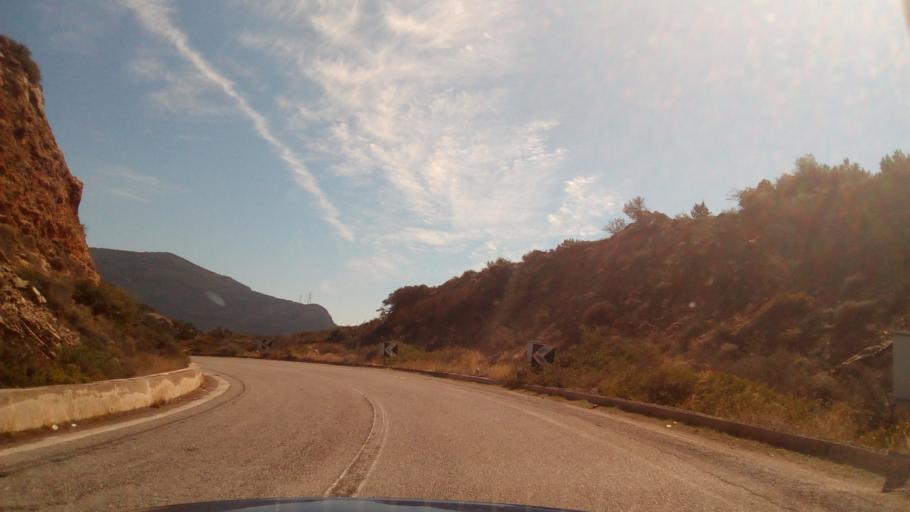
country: GR
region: West Greece
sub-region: Nomos Achaias
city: Selianitika
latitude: 38.3709
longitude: 22.1047
